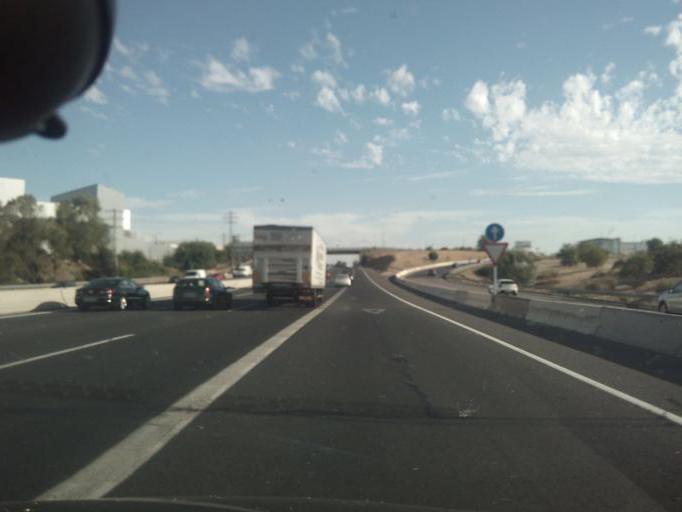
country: ES
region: Madrid
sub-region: Provincia de Madrid
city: Pinto
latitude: 40.2706
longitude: -3.6911
